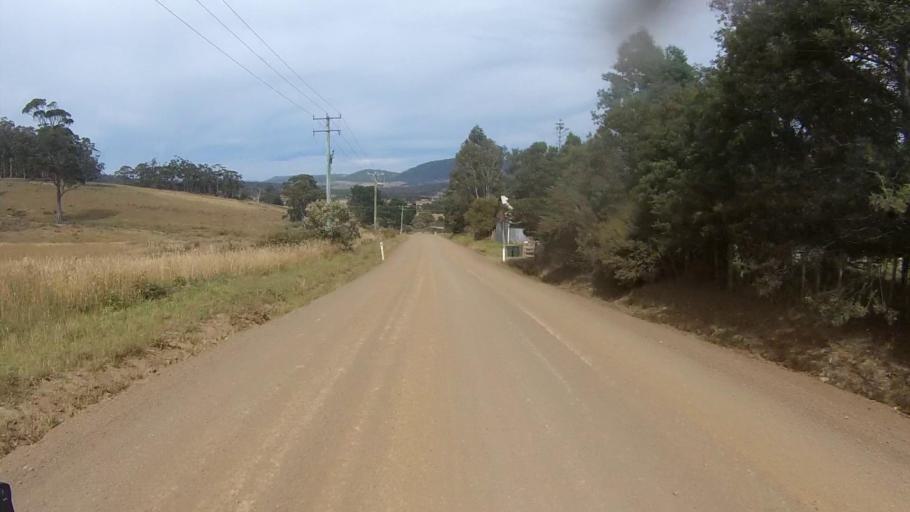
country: AU
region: Tasmania
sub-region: Sorell
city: Sorell
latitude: -42.7798
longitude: 147.8124
